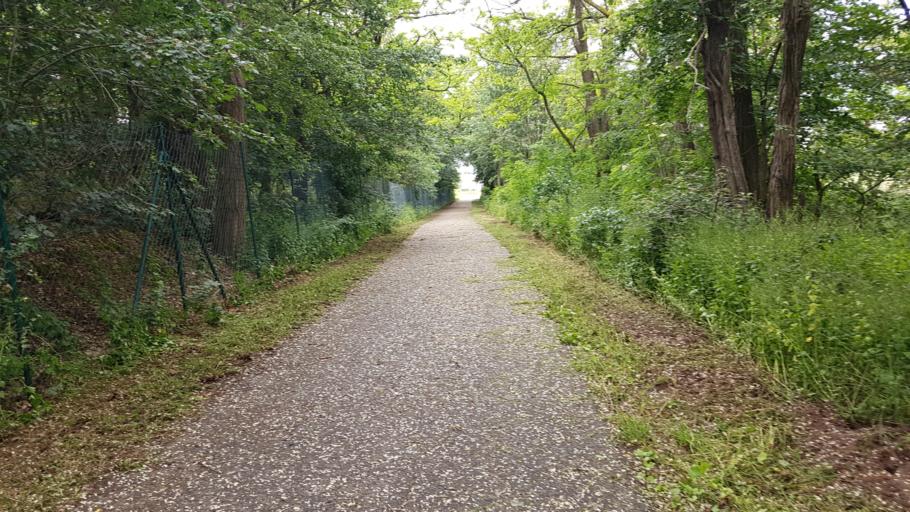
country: DE
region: Brandenburg
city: Finsterwalde
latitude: 51.6129
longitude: 13.7347
